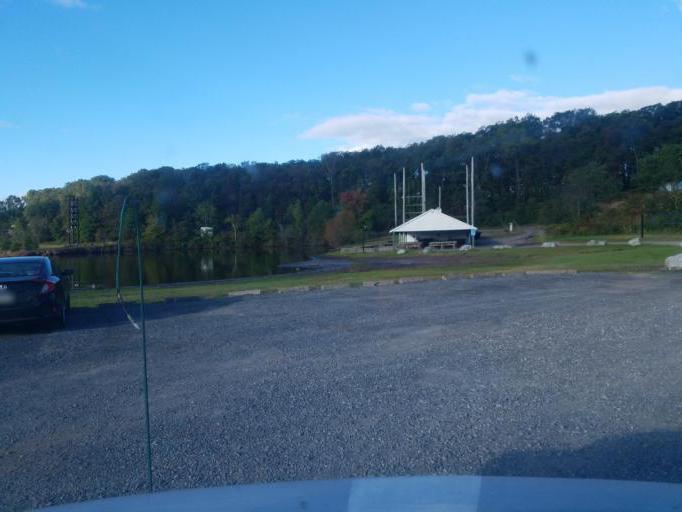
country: US
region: Pennsylvania
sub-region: Adams County
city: Gettysburg
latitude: 39.8386
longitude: -77.2409
